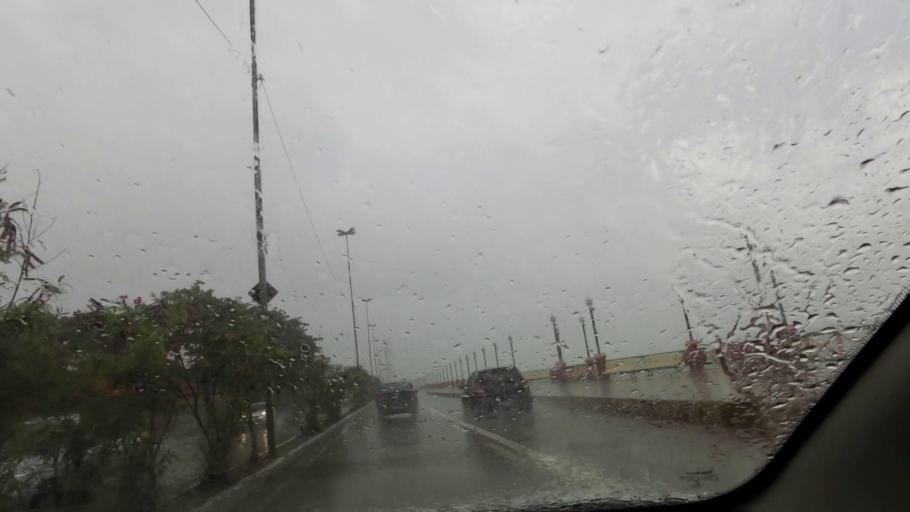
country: BR
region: Pernambuco
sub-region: Recife
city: Recife
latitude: -8.0765
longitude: -34.8892
